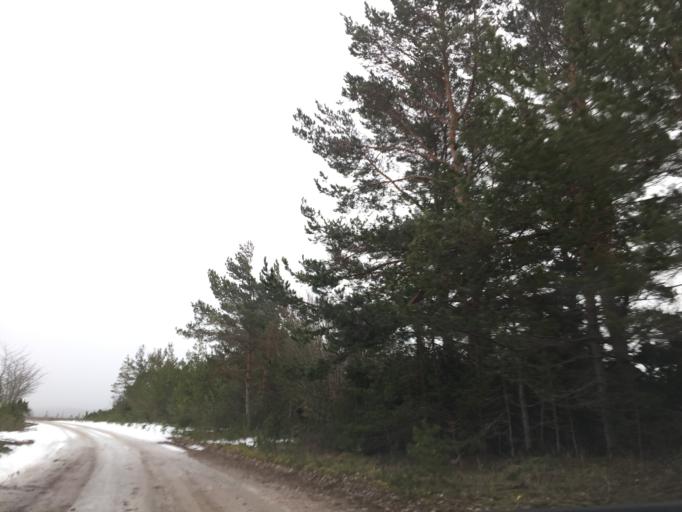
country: EE
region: Saare
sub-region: Kuressaare linn
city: Kuressaare
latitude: 58.5095
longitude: 21.9492
